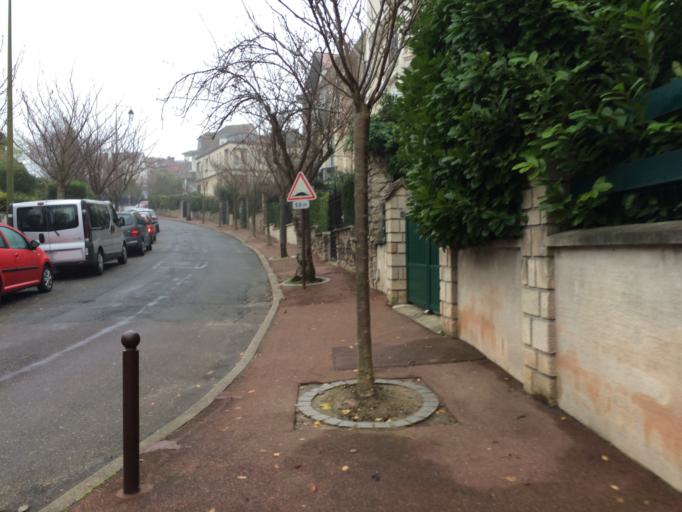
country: FR
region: Ile-de-France
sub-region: Departement des Hauts-de-Seine
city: Suresnes
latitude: 48.8597
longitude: 2.2171
